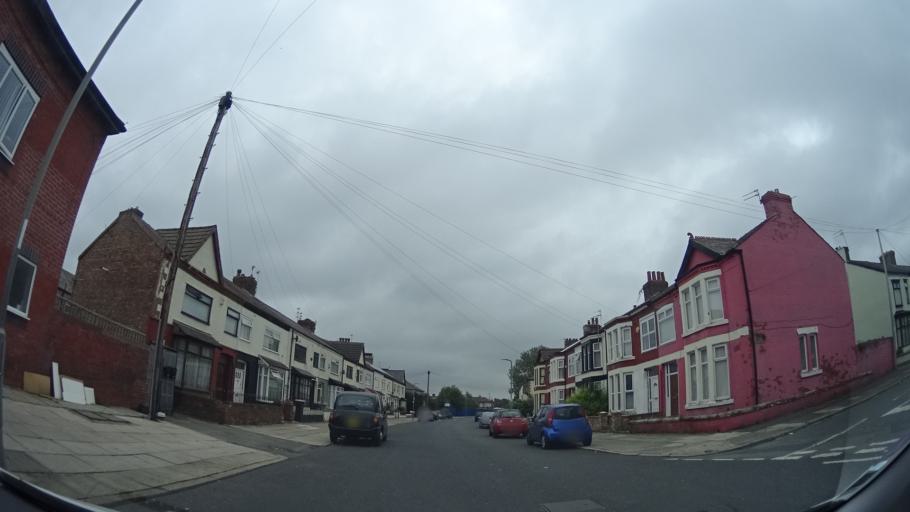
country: GB
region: England
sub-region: Sefton
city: Melling
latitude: 53.4194
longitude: -2.9143
